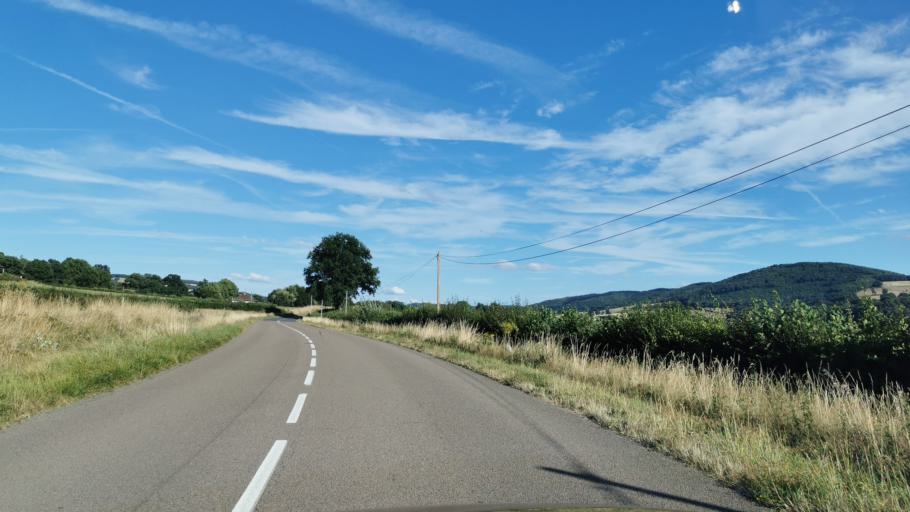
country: FR
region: Bourgogne
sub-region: Departement de Saone-et-Loire
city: Marmagne
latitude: 46.8546
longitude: 4.3183
